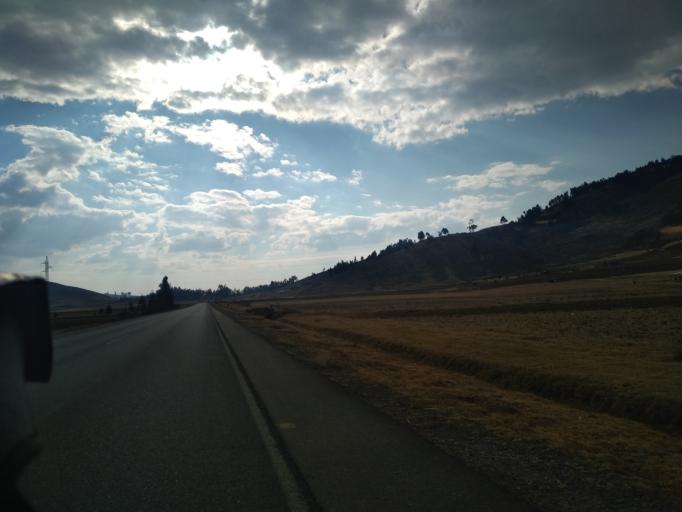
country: PE
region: Cajamarca
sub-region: Provincia de Cajamarca
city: Encanada
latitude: -7.1389
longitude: -78.3822
